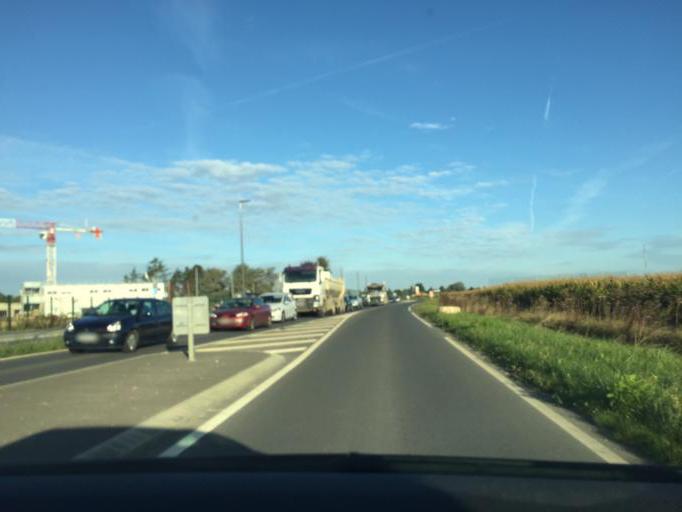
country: FR
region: Ile-de-France
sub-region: Departement de l'Essonne
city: Bures-sur-Yvette
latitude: 48.7114
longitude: 2.1508
